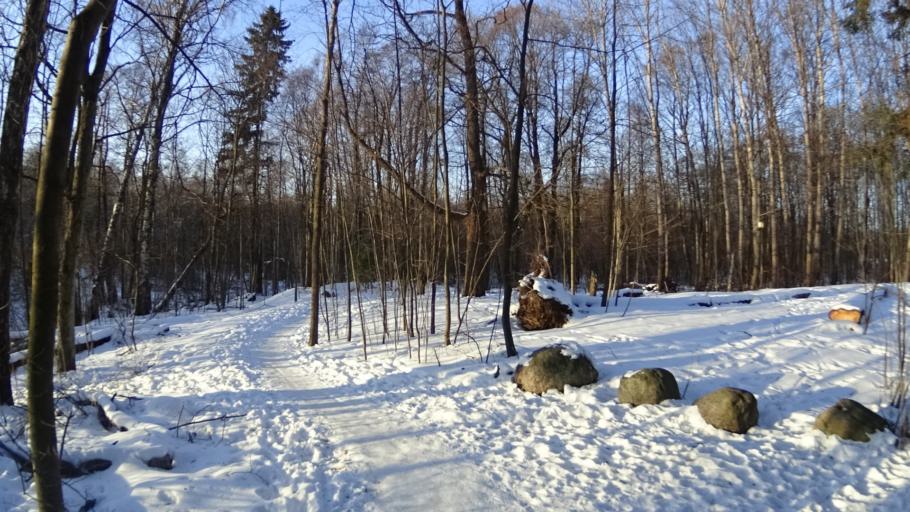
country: FI
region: Uusimaa
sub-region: Helsinki
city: Teekkarikylae
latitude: 60.2101
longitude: 24.8522
